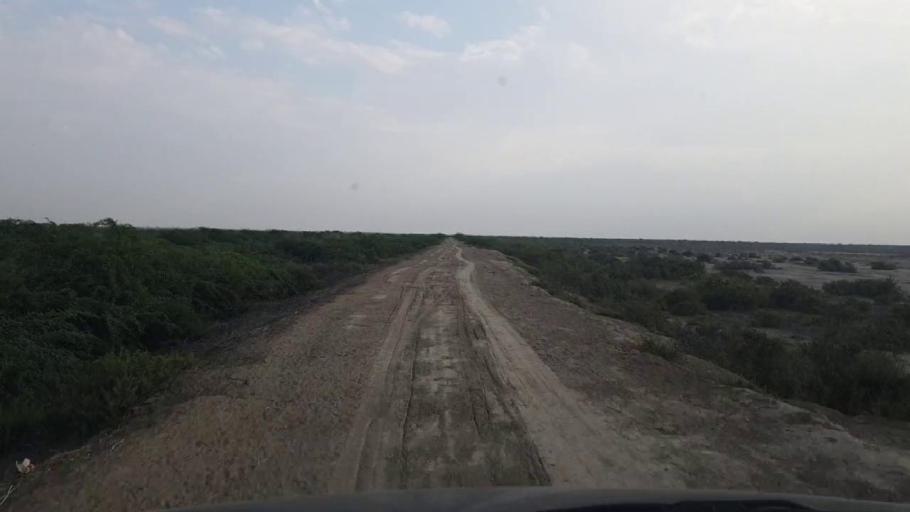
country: PK
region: Sindh
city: Badin
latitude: 24.4810
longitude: 68.6985
